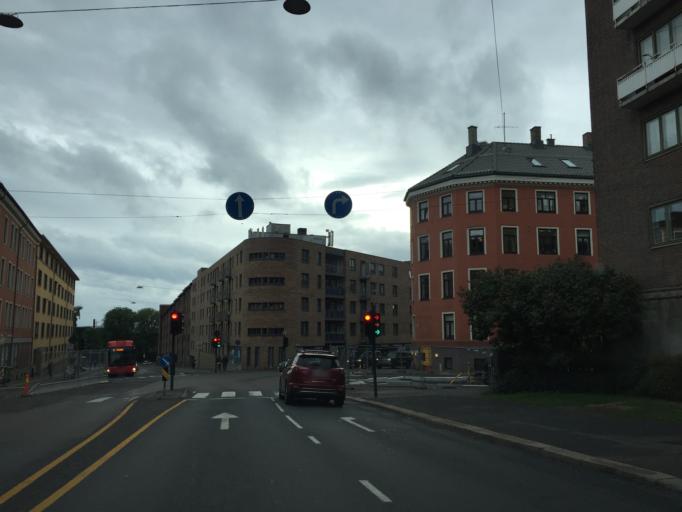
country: NO
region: Oslo
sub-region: Oslo
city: Oslo
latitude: 59.9292
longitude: 10.7679
